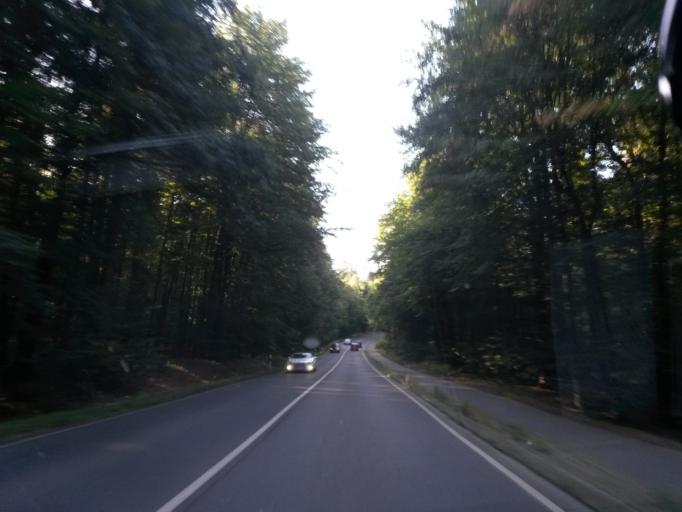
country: DE
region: North Rhine-Westphalia
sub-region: Regierungsbezirk Koln
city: Bergisch Gladbach
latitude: 50.9503
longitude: 7.1690
